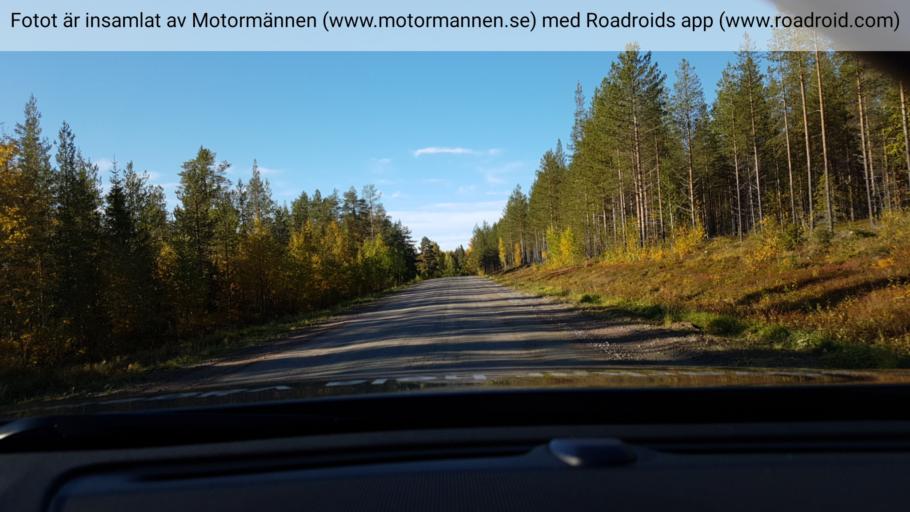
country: SE
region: Norrbotten
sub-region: Alvsbyns Kommun
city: AElvsbyn
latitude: 66.2666
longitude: 21.0864
